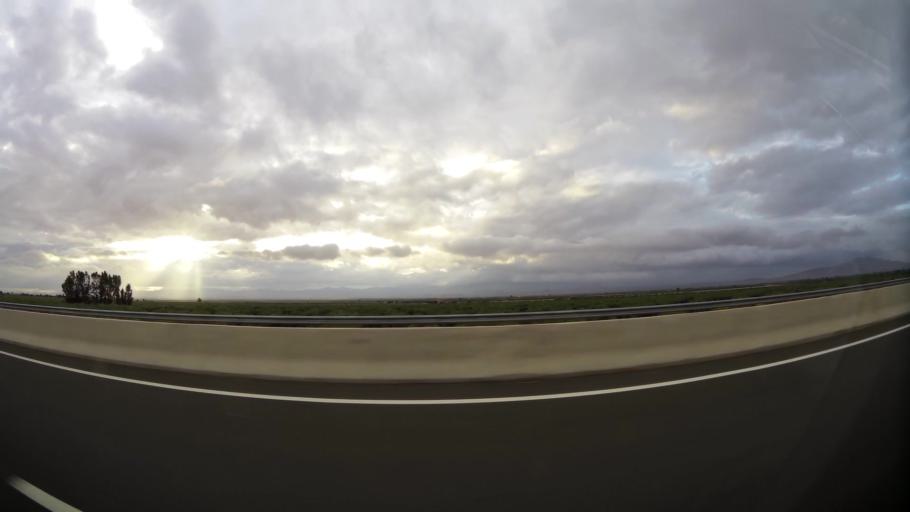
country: MA
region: Taza-Al Hoceima-Taounate
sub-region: Taza
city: Guercif
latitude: 34.3321
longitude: -3.3378
